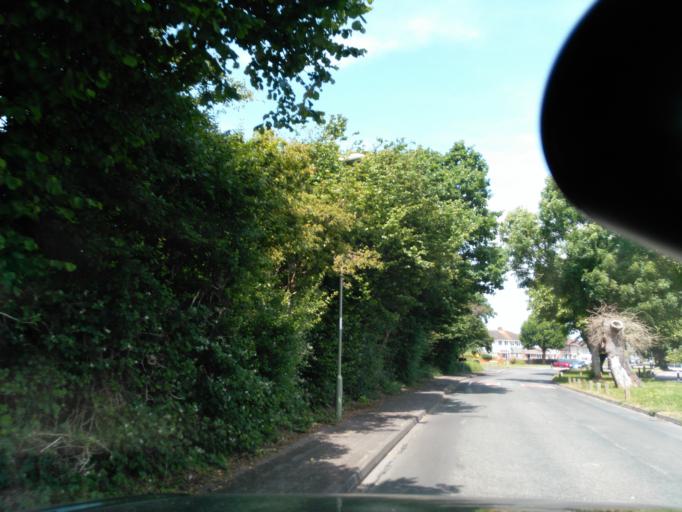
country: GB
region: England
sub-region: Hampshire
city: Fareham
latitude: 50.8242
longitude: -1.1773
